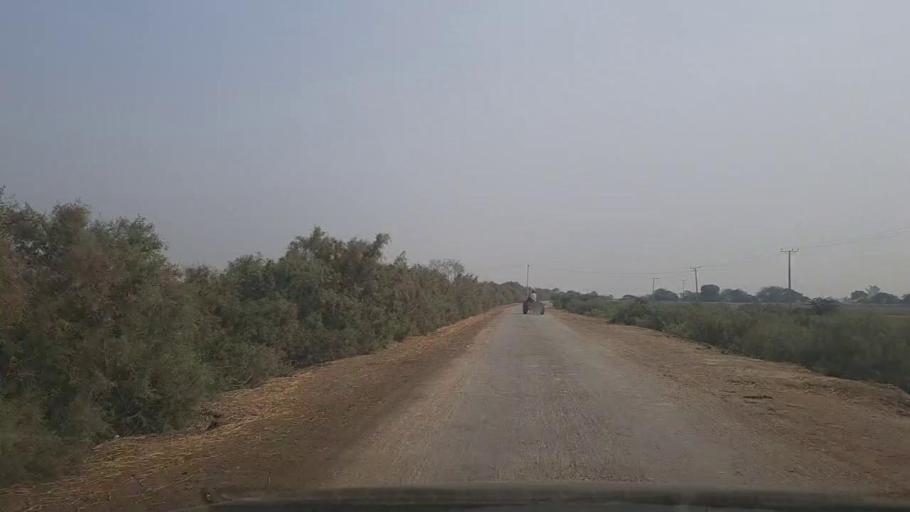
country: PK
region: Sindh
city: Mirpur Sakro
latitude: 24.4787
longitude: 67.6570
